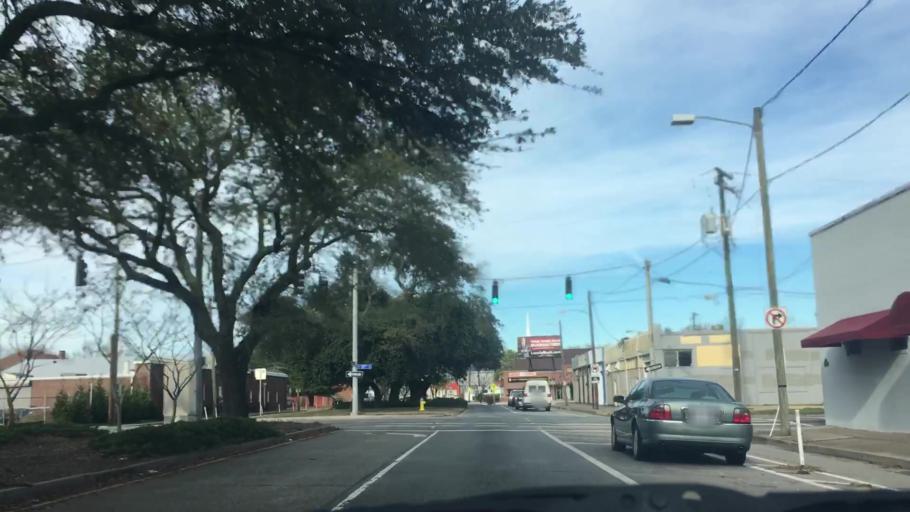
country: US
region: Virginia
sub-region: City of Norfolk
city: Norfolk
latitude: 36.8748
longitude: -76.2950
